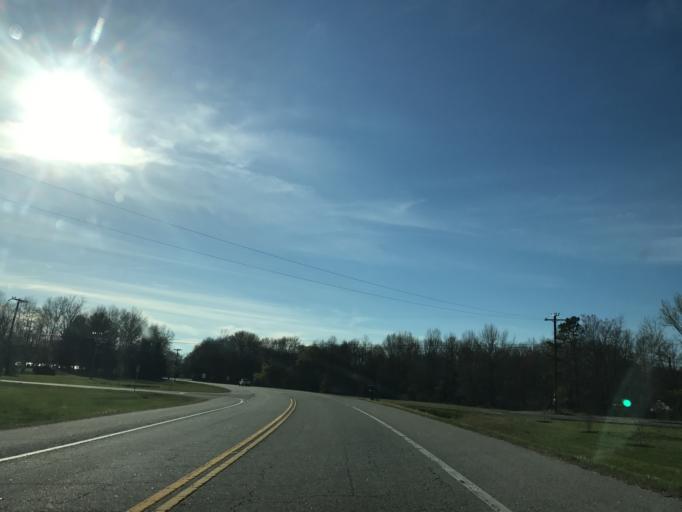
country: US
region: Maryland
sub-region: Caroline County
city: Greensboro
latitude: 39.1155
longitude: -75.7495
